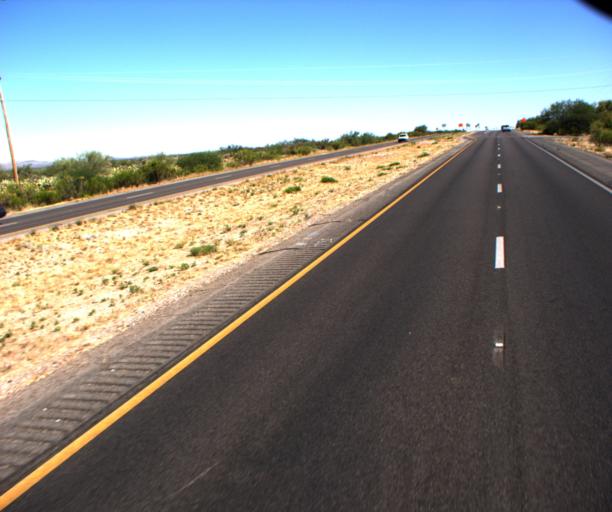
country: US
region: Arizona
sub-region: Pima County
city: Catalina
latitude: 32.5163
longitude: -110.9263
